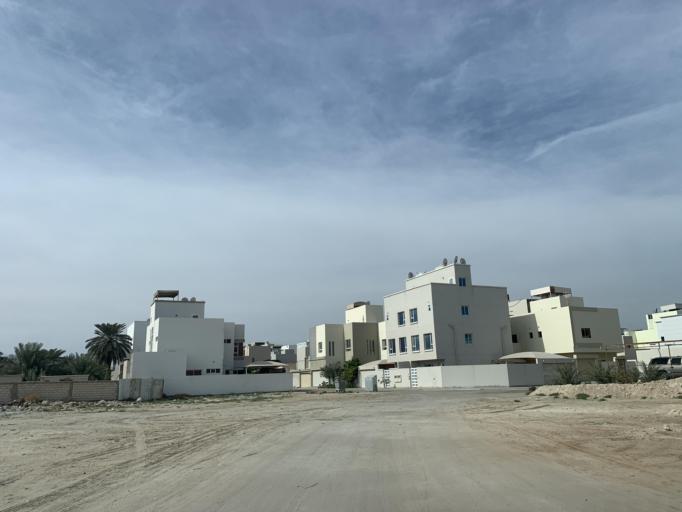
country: BH
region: Central Governorate
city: Madinat Hamad
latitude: 26.1287
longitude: 50.4738
